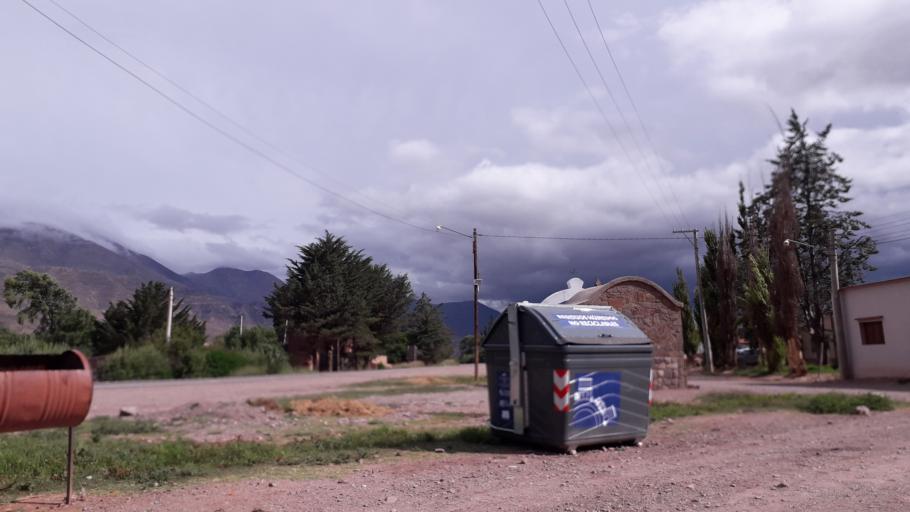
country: AR
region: Jujuy
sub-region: Departamento de Humahuaca
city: Humahuaca
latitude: -23.3050
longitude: -65.3550
